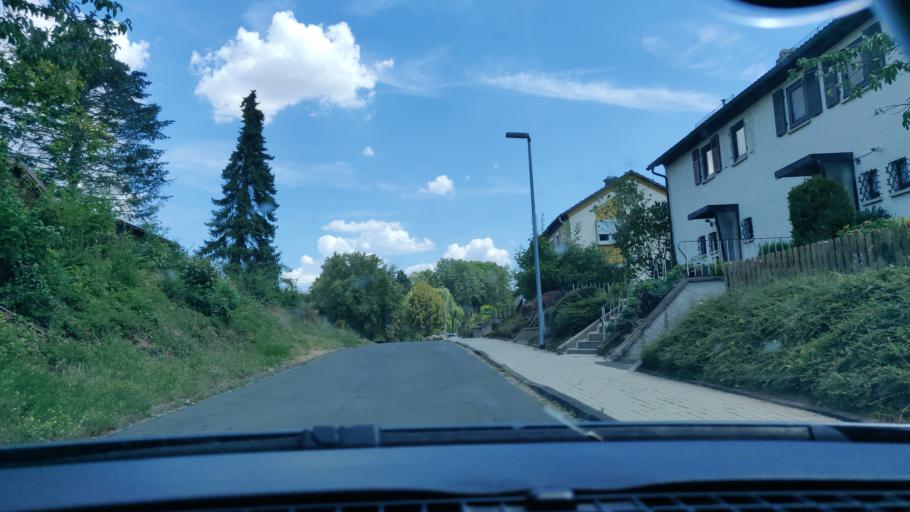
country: DE
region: Hesse
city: Fritzlar
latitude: 51.1307
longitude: 9.2872
